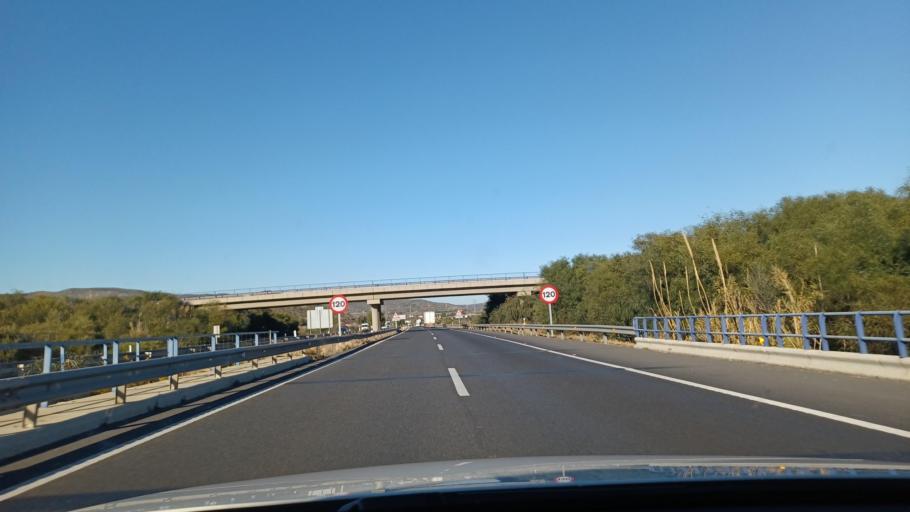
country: ES
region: Valencia
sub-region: Provincia de Castello
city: Orpesa/Oropesa del Mar
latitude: 40.1380
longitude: 0.1422
